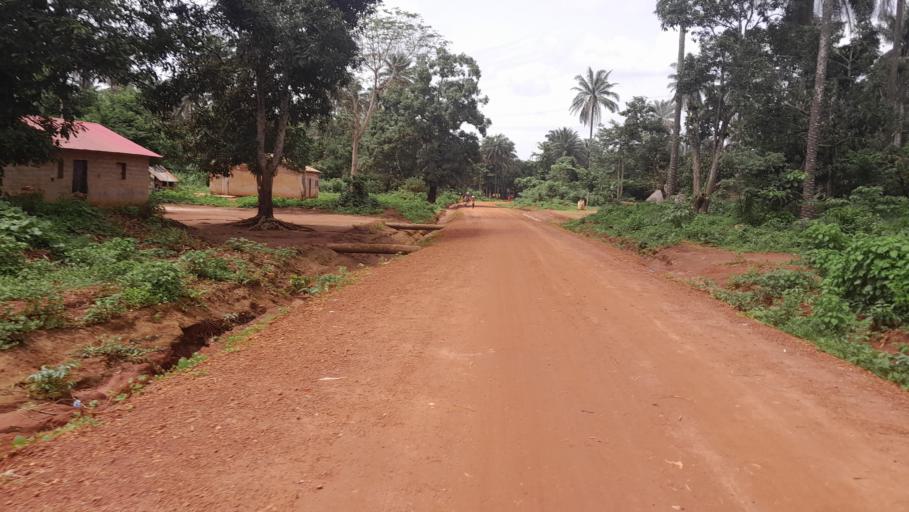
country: GN
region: Boke
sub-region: Boffa
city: Boffa
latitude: 10.0048
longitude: -13.8860
